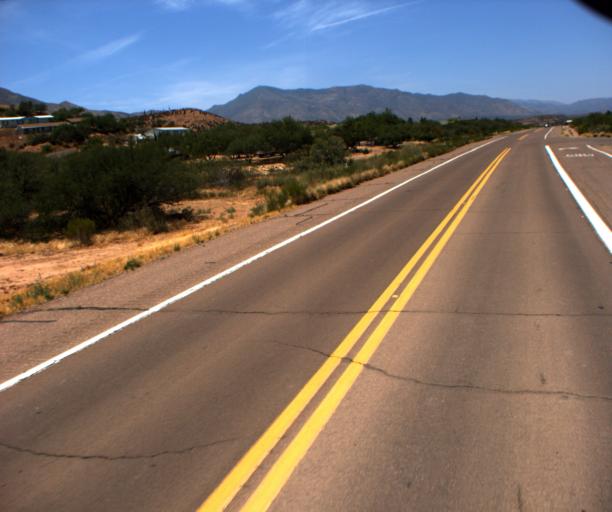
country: US
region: Arizona
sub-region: Gila County
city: Tonto Basin
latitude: 33.8333
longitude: -111.3000
